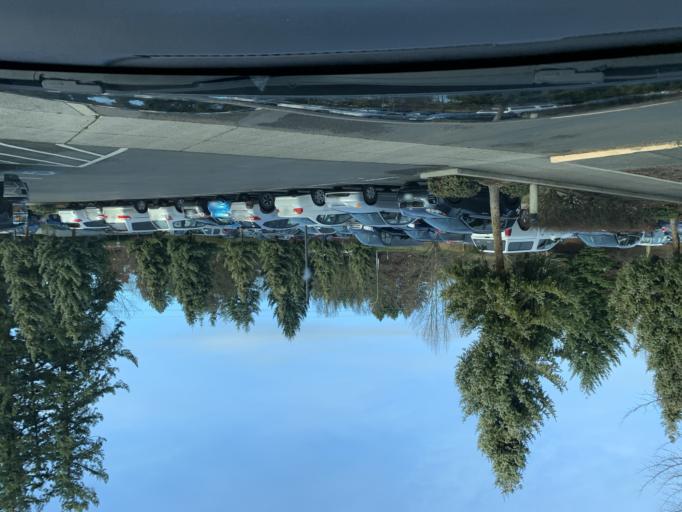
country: US
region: Washington
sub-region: Clark County
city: Mill Plain
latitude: 45.5949
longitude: -122.5053
